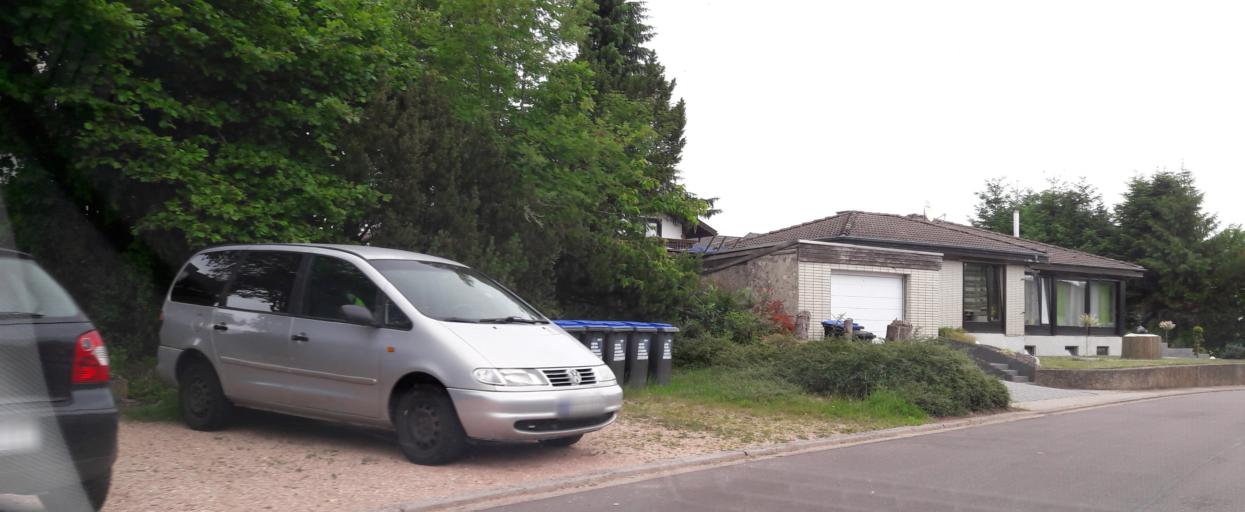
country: DE
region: Saarland
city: Oberthal
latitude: 49.5508
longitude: 7.0562
